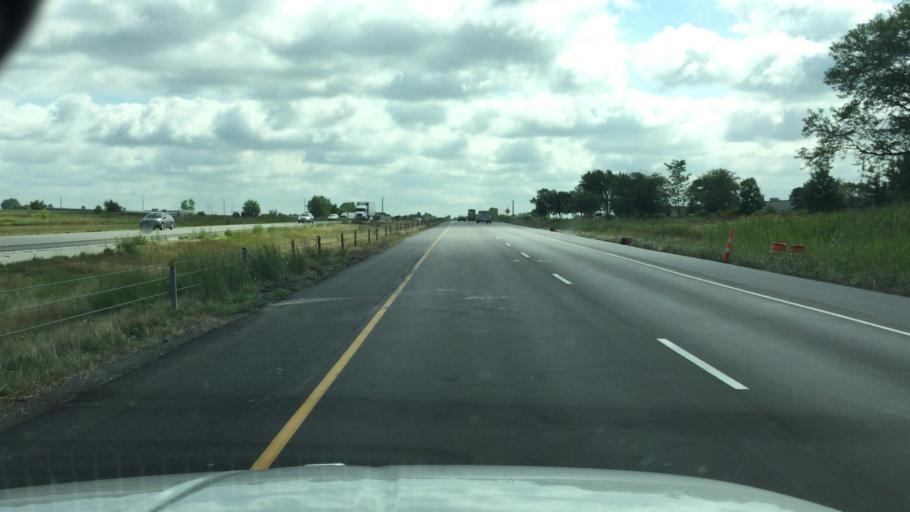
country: US
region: Iowa
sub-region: Scott County
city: Eldridge
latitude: 41.5998
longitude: -90.6183
